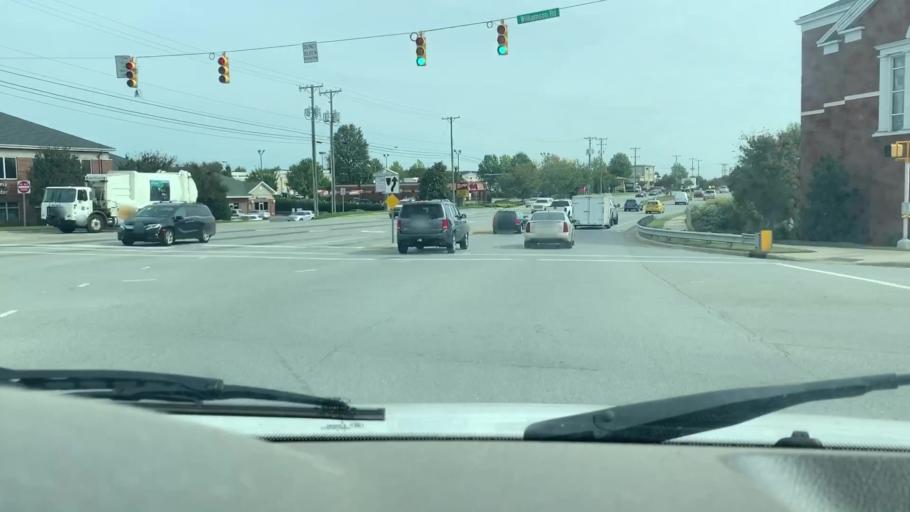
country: US
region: North Carolina
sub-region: Iredell County
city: Mooresville
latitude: 35.5839
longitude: -80.8737
